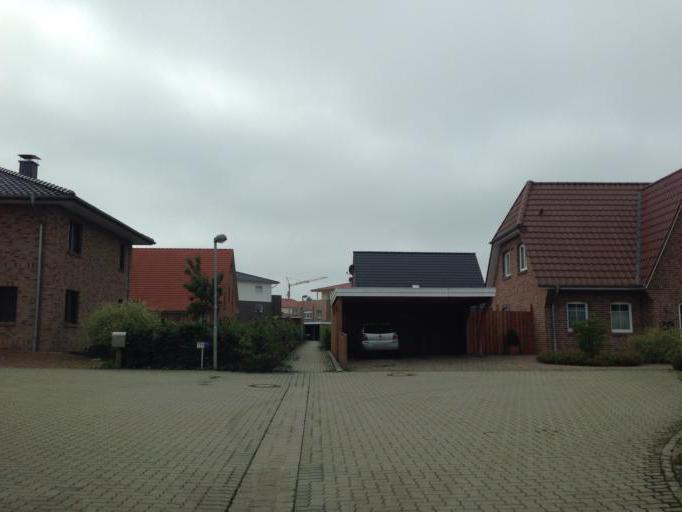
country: DE
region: Lower Saxony
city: Adendorf
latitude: 53.2907
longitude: 10.4364
